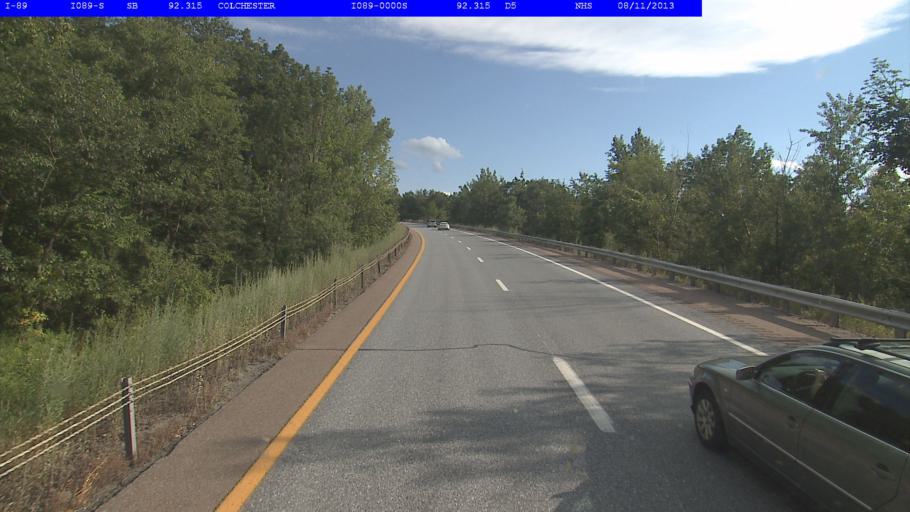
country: US
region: Vermont
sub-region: Chittenden County
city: Winooski
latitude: 44.5140
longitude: -73.1921
